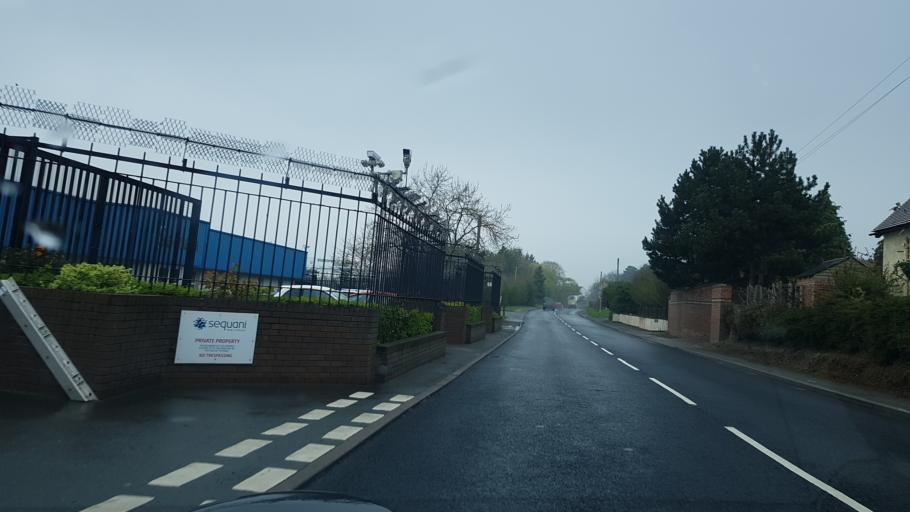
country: GB
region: England
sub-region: Herefordshire
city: Ledbury
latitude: 52.0462
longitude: -2.4268
